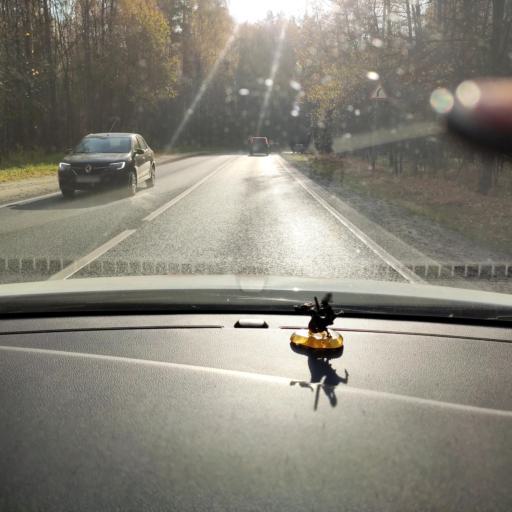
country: RU
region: Tatarstan
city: Osinovo
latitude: 55.8396
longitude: 48.8931
